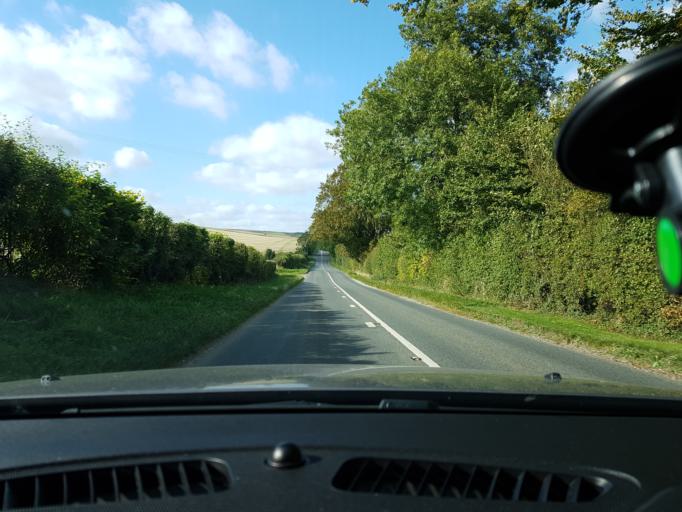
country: GB
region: England
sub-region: Wiltshire
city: Aldbourne
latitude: 51.4973
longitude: -1.6554
